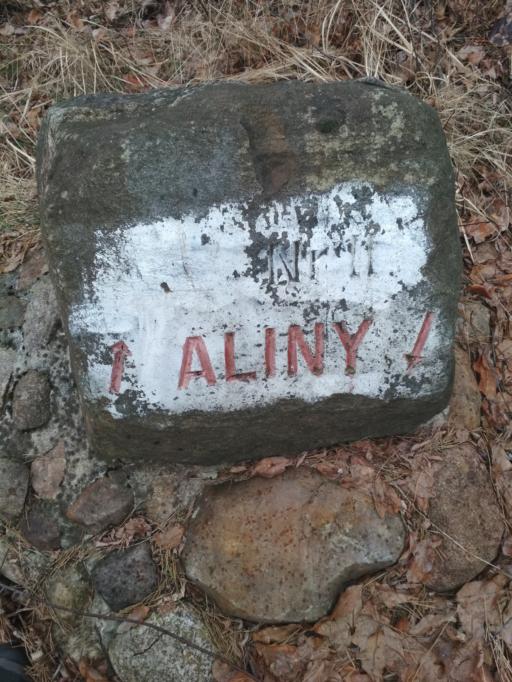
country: PL
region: Lubusz
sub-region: Powiat zielonogorski
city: Nowogrod Bobrzanski
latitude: 51.8088
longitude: 15.1977
